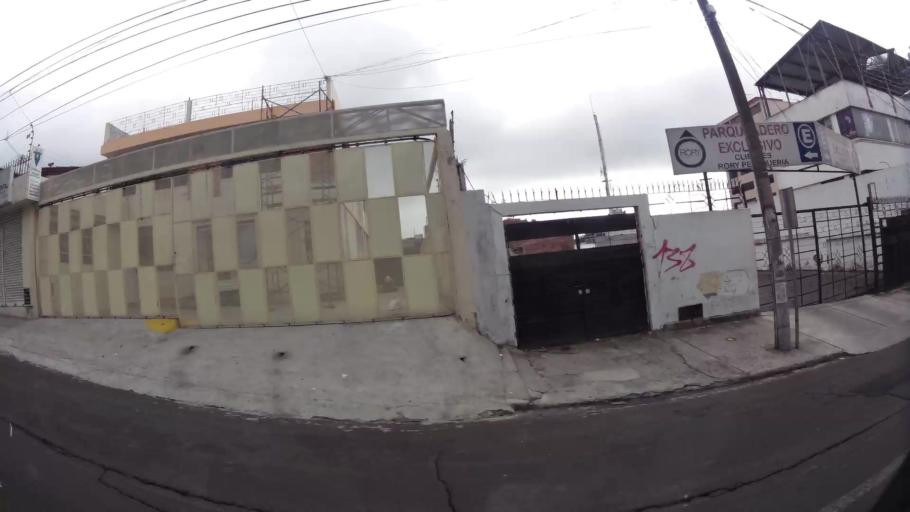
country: EC
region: Pichincha
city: Quito
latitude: -0.1877
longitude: -78.4926
